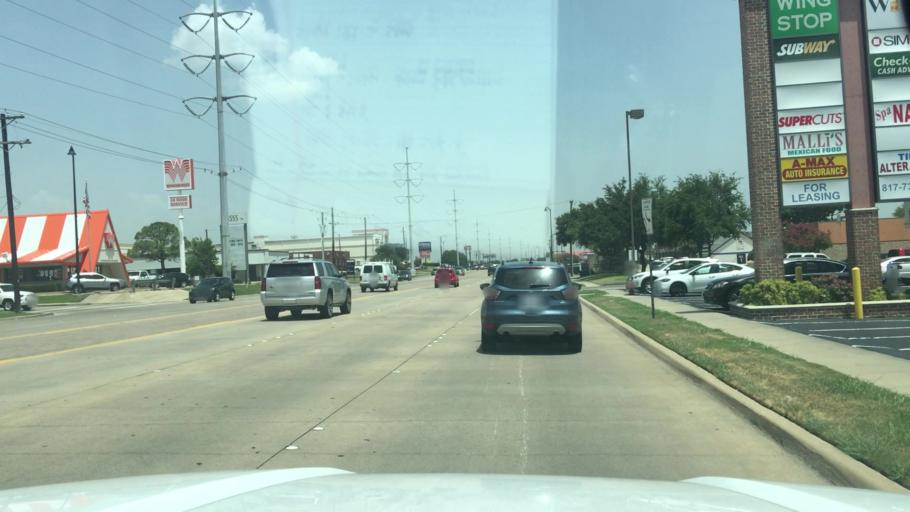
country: US
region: Texas
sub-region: Tarrant County
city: North Richland Hills
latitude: 32.8464
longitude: -97.2385
